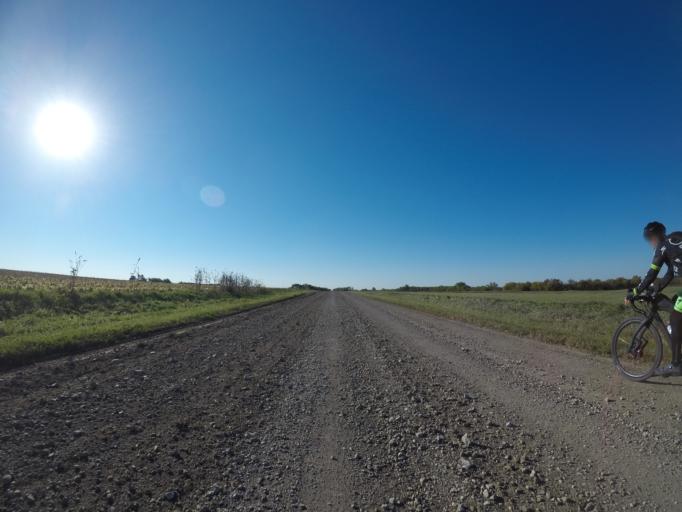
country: US
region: Kansas
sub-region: Morris County
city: Council Grove
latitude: 38.8588
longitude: -96.4829
